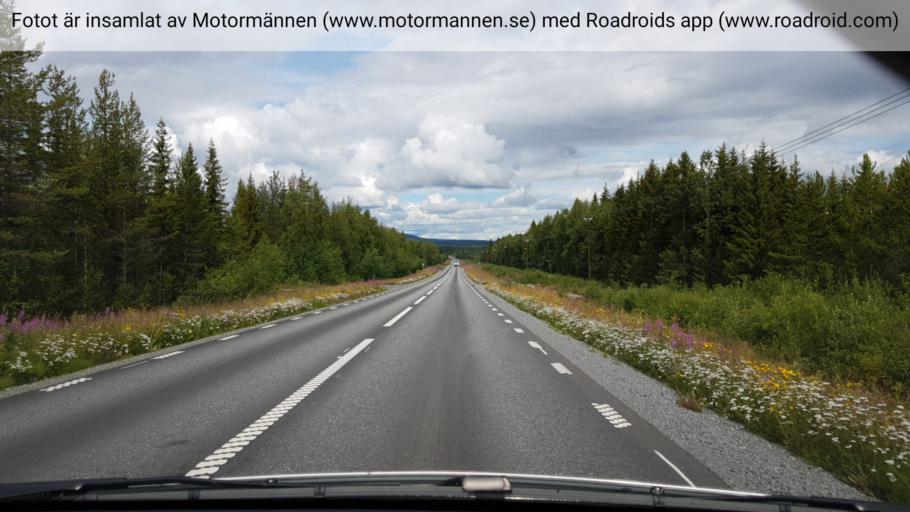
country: SE
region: Vaesterbotten
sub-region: Vilhelmina Kommun
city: Vilhelmina
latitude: 64.7185
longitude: 16.7069
